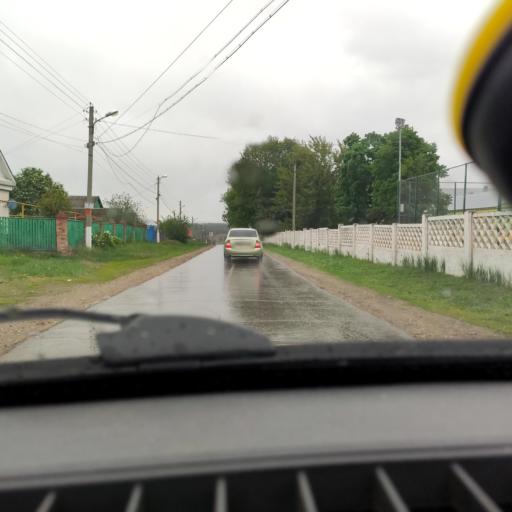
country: RU
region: Samara
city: Zhigulevsk
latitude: 53.5509
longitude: 49.5273
